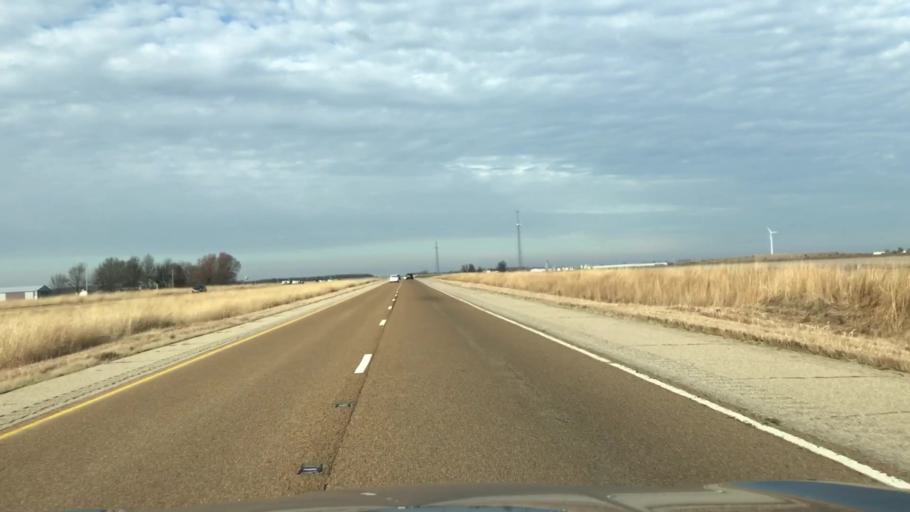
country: US
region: Illinois
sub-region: Montgomery County
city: Raymond
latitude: 39.4112
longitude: -89.6432
